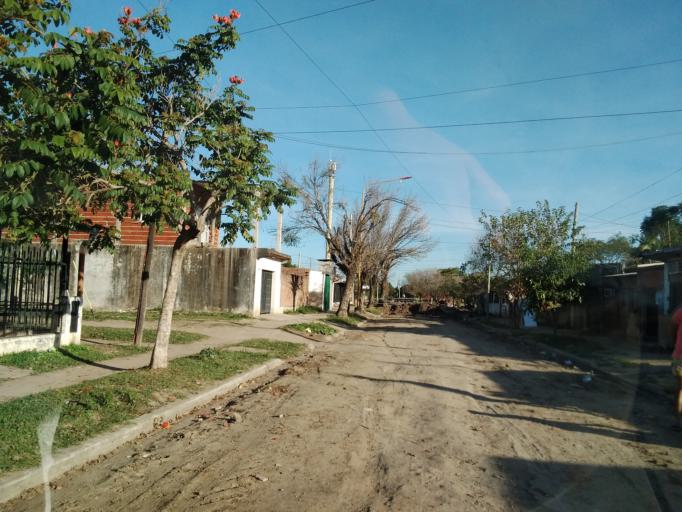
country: AR
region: Corrientes
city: Corrientes
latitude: -27.5034
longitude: -58.8360
